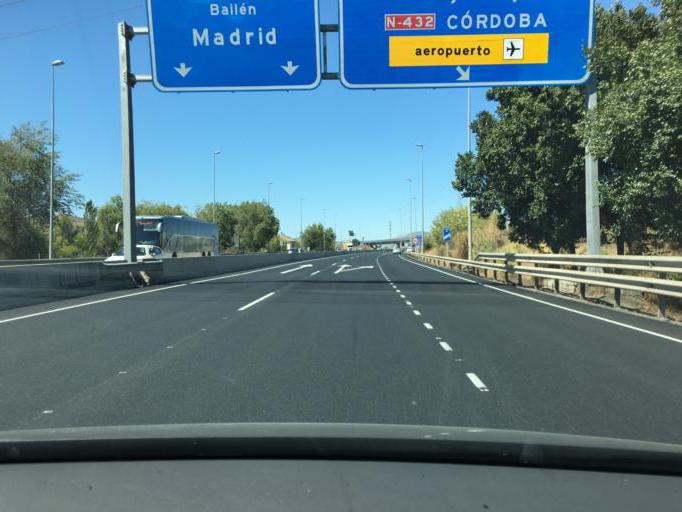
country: ES
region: Andalusia
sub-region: Provincia de Granada
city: Albolote
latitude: 37.2383
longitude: -3.6485
